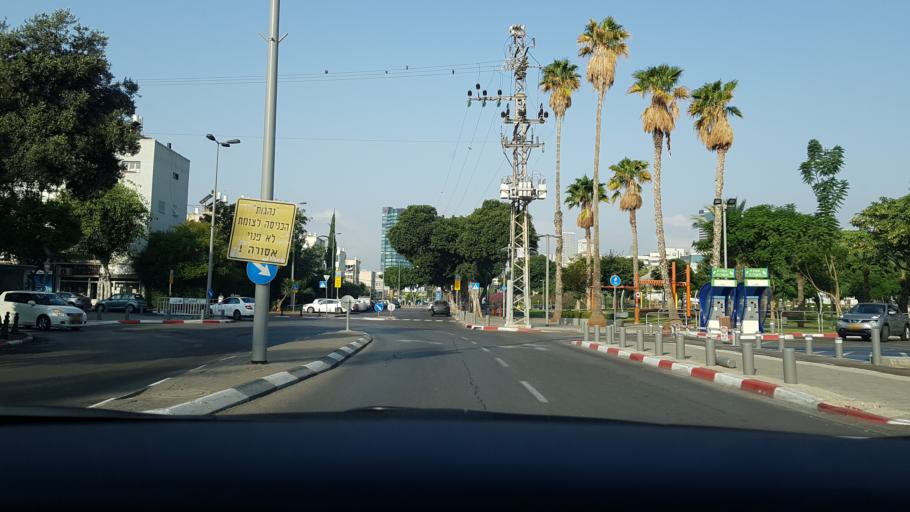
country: IL
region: Tel Aviv
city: Tel Aviv
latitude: 32.0601
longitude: 34.7899
